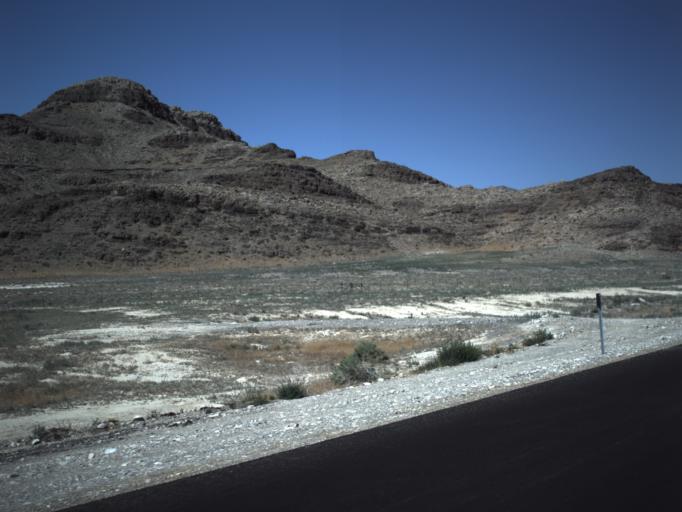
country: US
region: Utah
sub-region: Beaver County
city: Milford
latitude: 39.0613
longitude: -113.4397
